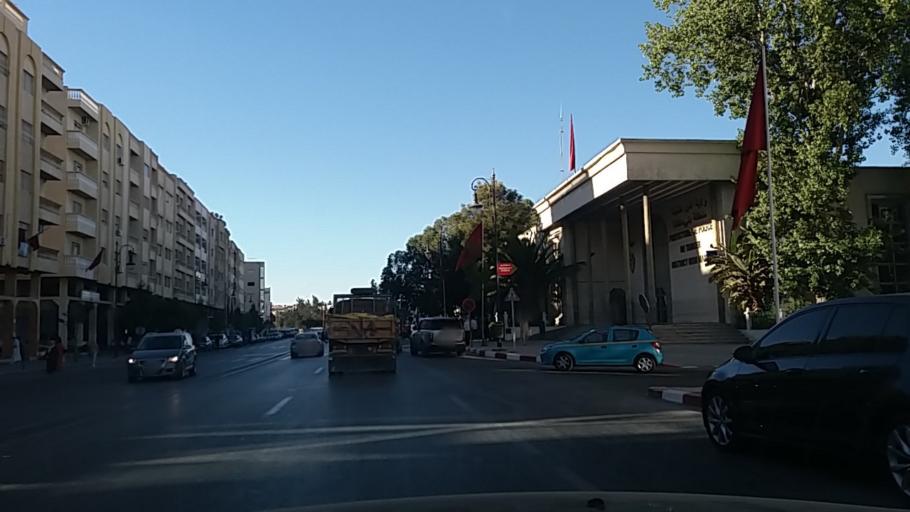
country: MA
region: Tanger-Tetouan
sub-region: Tanger-Assilah
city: Tangier
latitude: 35.7471
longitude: -5.7987
